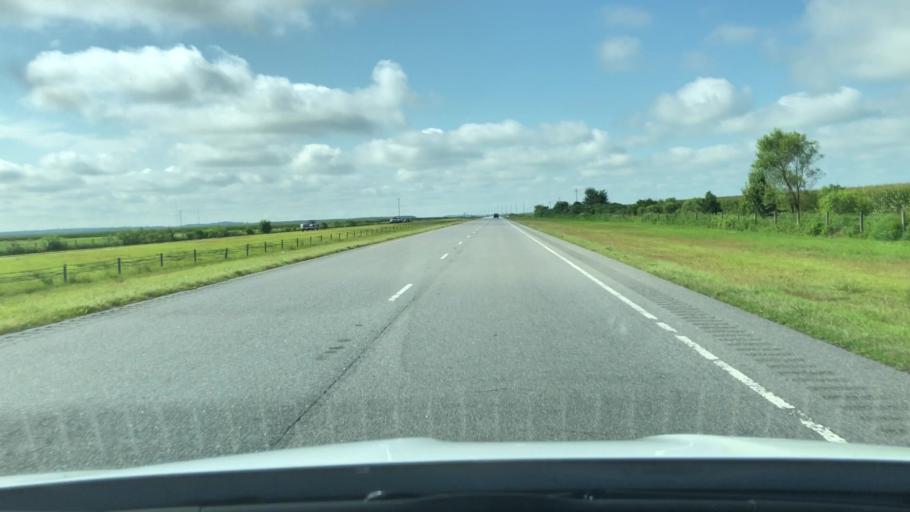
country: US
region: North Carolina
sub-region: Pasquotank County
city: Elizabeth City
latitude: 36.3450
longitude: -76.3136
